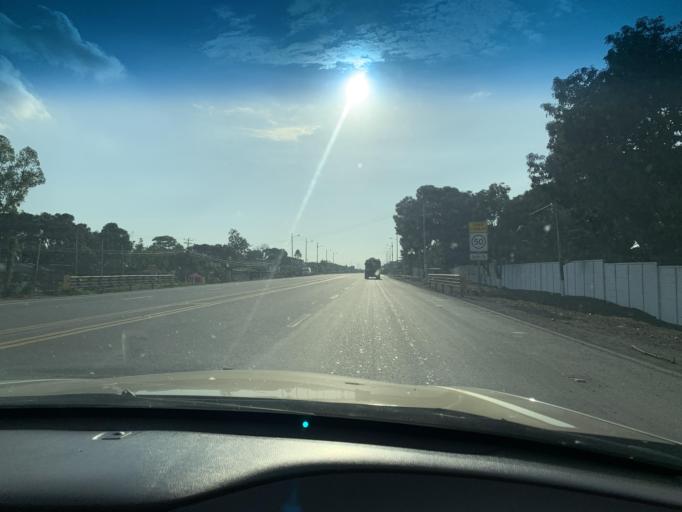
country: EC
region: Guayas
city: Naranjito
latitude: -2.2562
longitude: -79.5949
